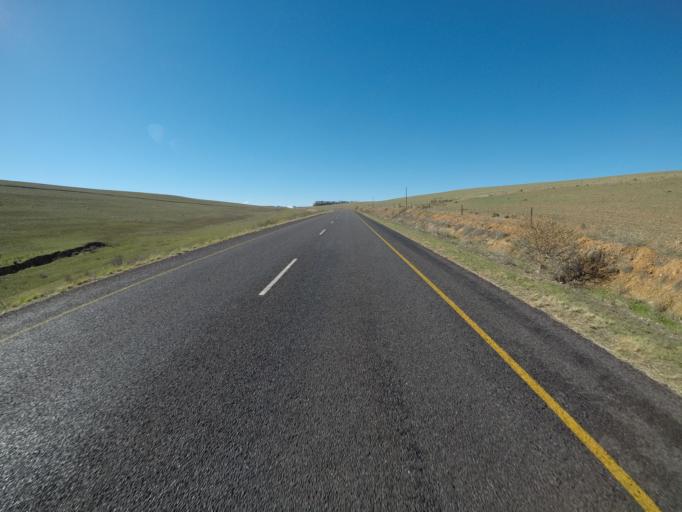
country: ZA
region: Western Cape
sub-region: Overberg District Municipality
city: Caledon
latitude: -34.1454
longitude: 19.4944
